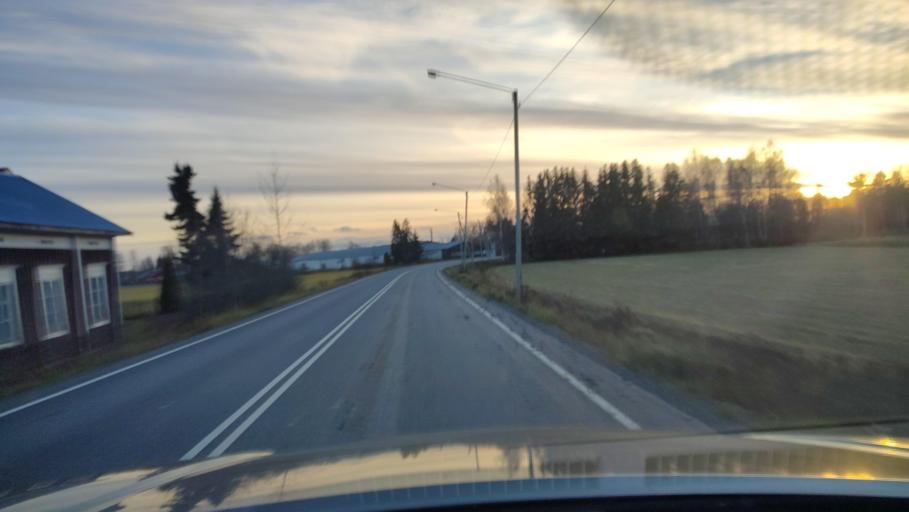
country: FI
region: Ostrobothnia
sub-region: Sydosterbotten
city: Kristinestad
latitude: 62.2649
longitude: 21.5414
